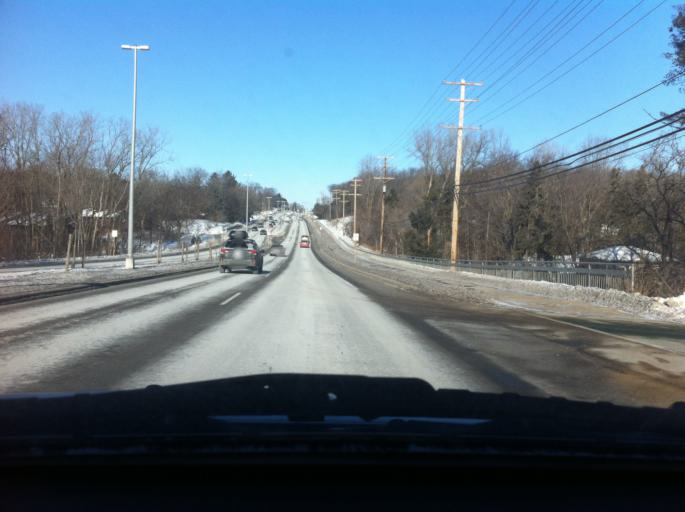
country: US
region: Wisconsin
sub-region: Dane County
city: Middleton
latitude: 43.0860
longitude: -89.4797
